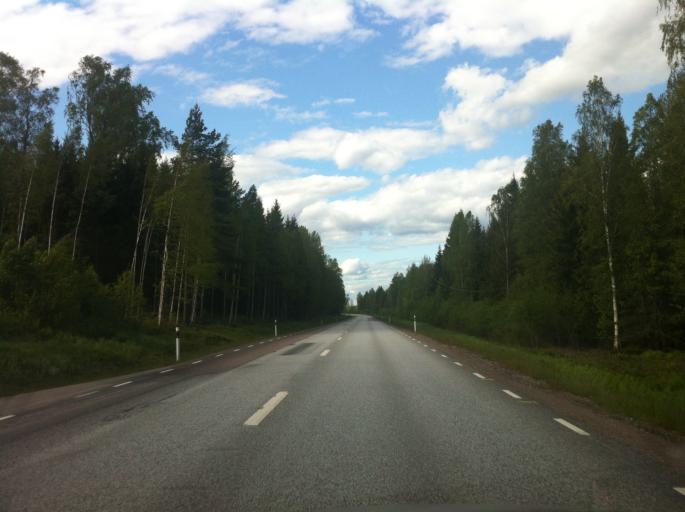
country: SE
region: Vaermland
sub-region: Storfors Kommun
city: Storfors
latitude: 59.4759
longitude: 14.2578
